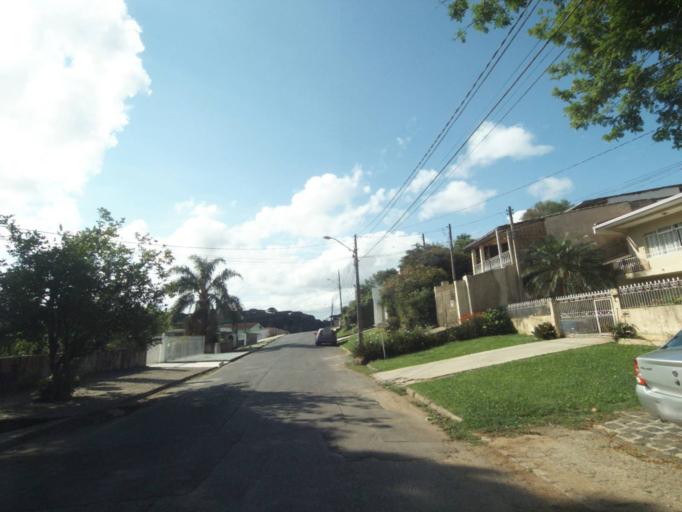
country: BR
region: Parana
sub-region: Curitiba
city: Curitiba
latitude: -25.3911
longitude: -49.3014
